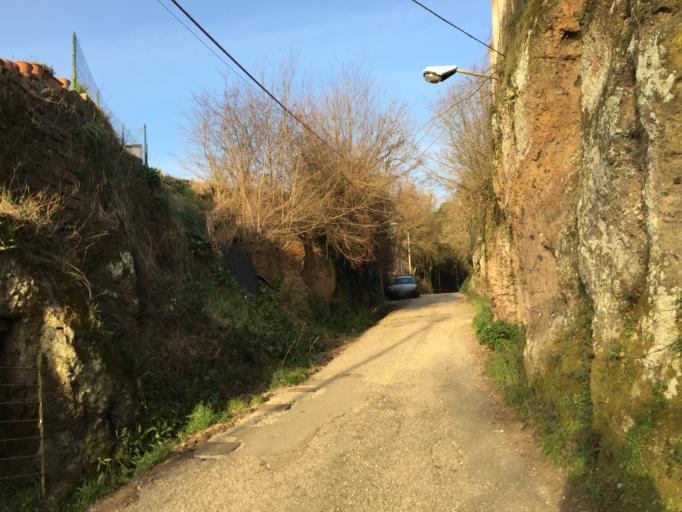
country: IT
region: Latium
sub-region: Provincia di Viterbo
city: Calcata Nuova
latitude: 42.2173
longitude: 12.4216
